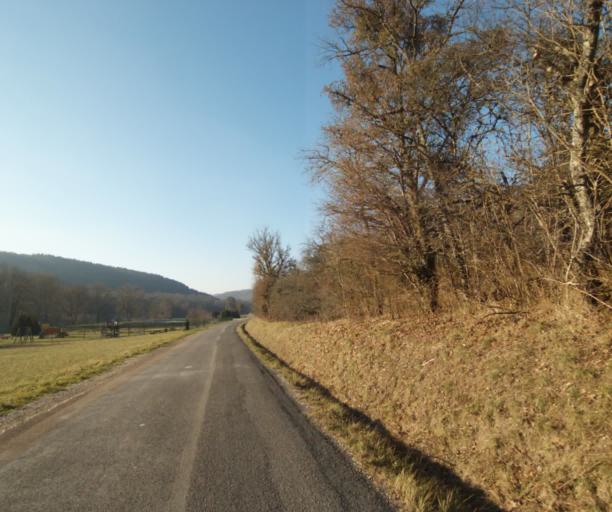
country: FR
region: Champagne-Ardenne
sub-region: Departement de la Haute-Marne
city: Chevillon
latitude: 48.5002
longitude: 5.1864
